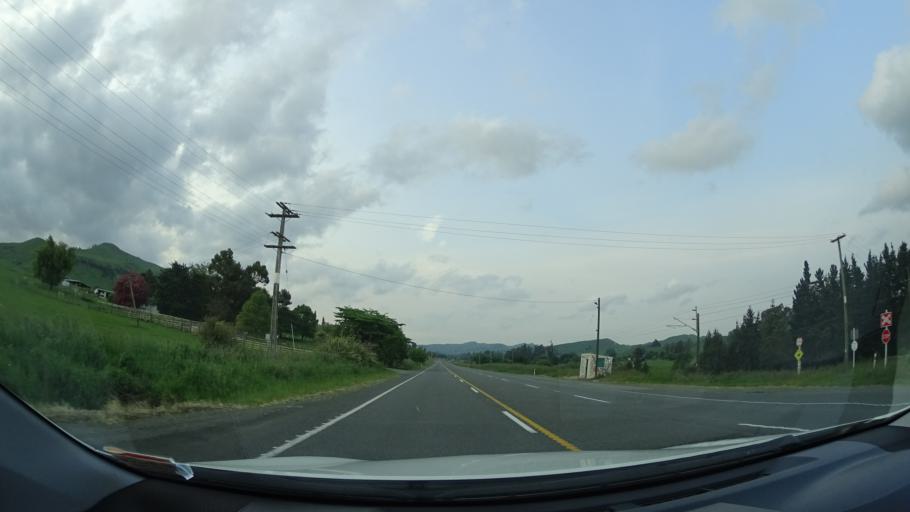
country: NZ
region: Manawatu-Wanganui
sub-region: Ruapehu District
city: Waiouru
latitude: -39.7246
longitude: 175.8417
